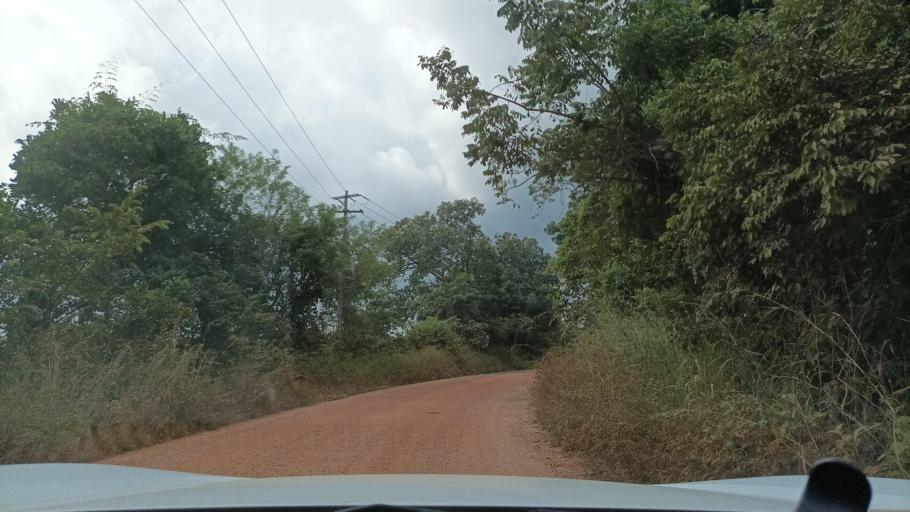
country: MX
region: Veracruz
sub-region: Chinameca
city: Chacalapa
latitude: 18.0822
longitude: -94.6827
